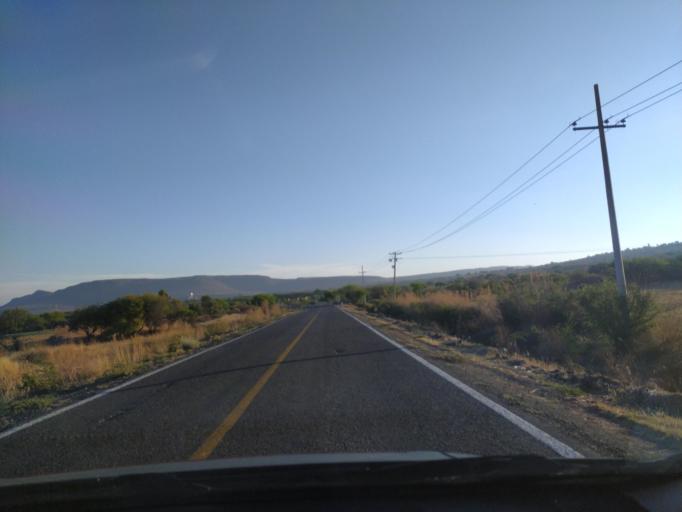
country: MX
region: Guanajuato
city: Ciudad Manuel Doblado
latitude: 20.7410
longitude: -101.8237
